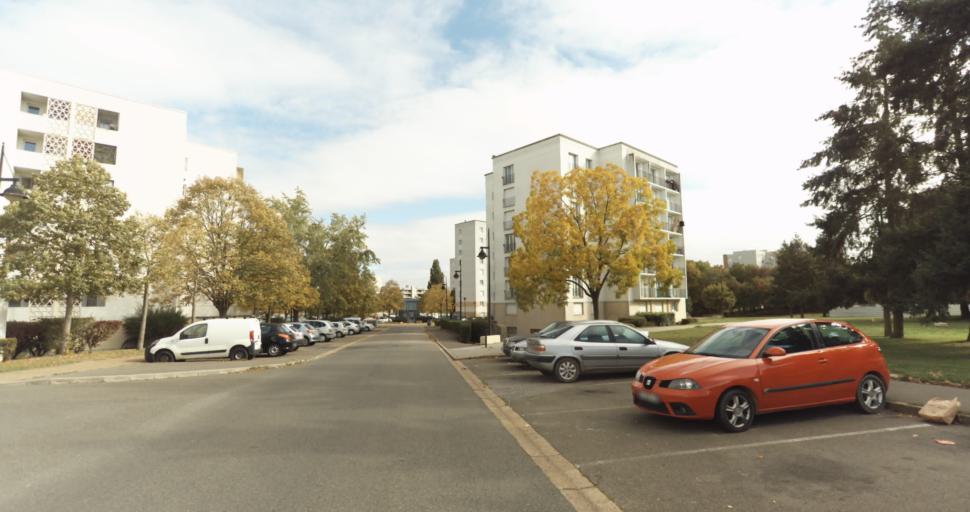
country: FR
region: Centre
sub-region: Departement d'Eure-et-Loir
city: Garnay
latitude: 48.7338
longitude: 1.3375
